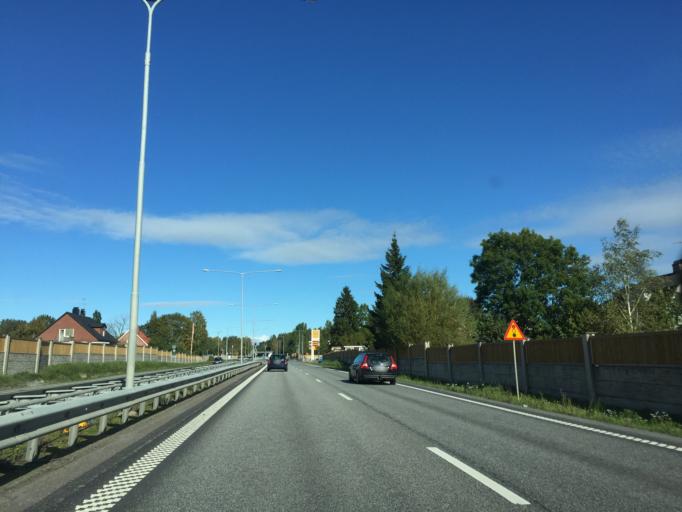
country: SE
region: OErebro
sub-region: Orebro Kommun
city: Hovsta
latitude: 59.3143
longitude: 15.2293
